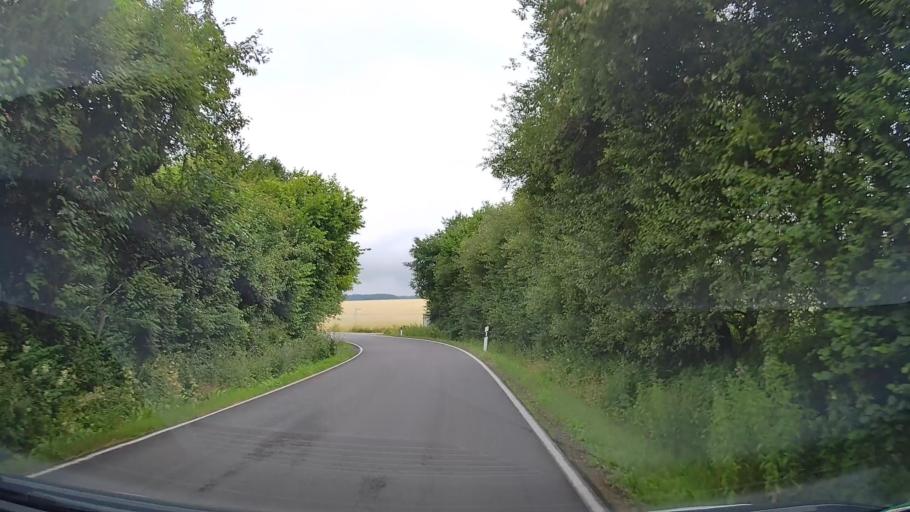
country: DE
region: Lower Saxony
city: Rinteln
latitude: 52.1106
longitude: 9.1204
